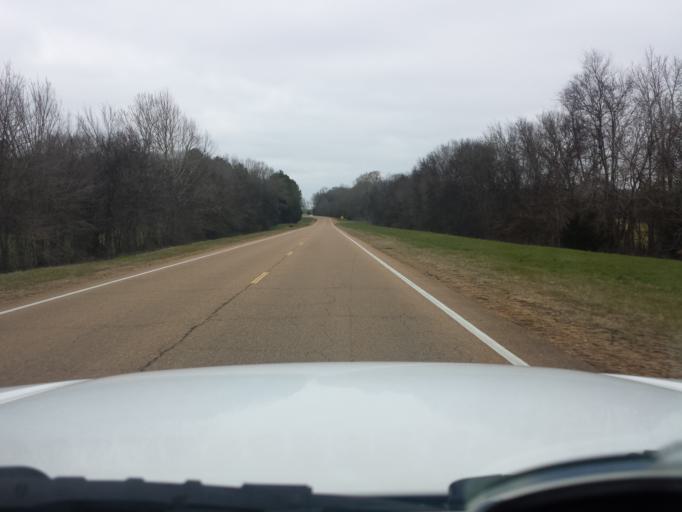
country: US
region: Mississippi
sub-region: Madison County
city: Canton
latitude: 32.7275
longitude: -90.1010
